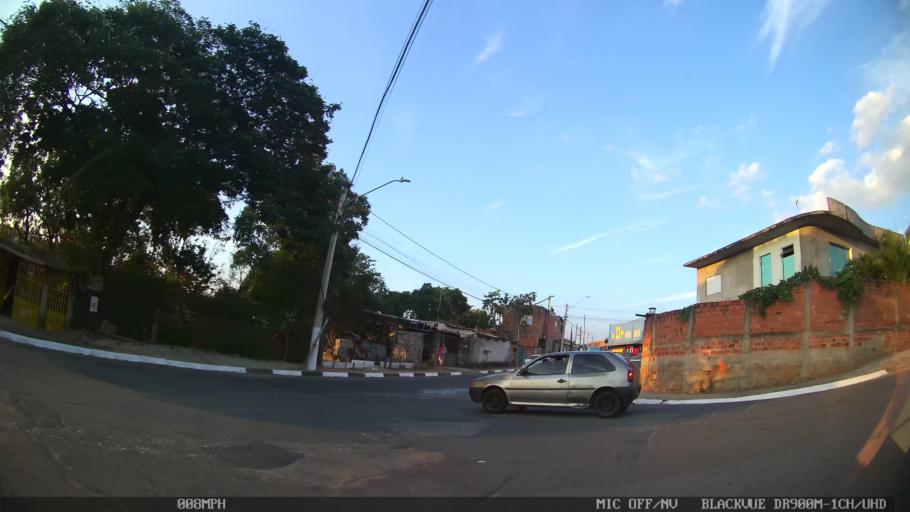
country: BR
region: Sao Paulo
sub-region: Hortolandia
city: Hortolandia
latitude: -22.8600
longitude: -47.2081
